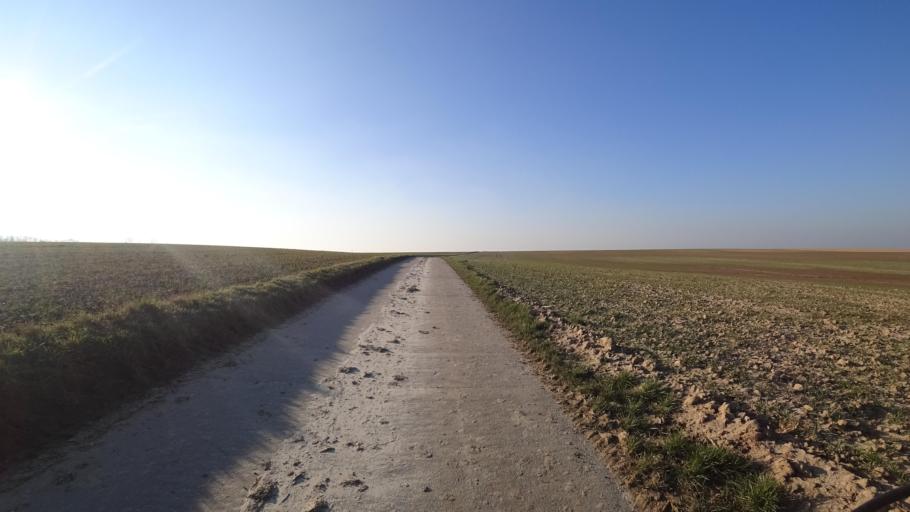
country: BE
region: Wallonia
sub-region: Province du Brabant Wallon
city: Chaumont-Gistoux
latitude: 50.6403
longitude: 4.7478
